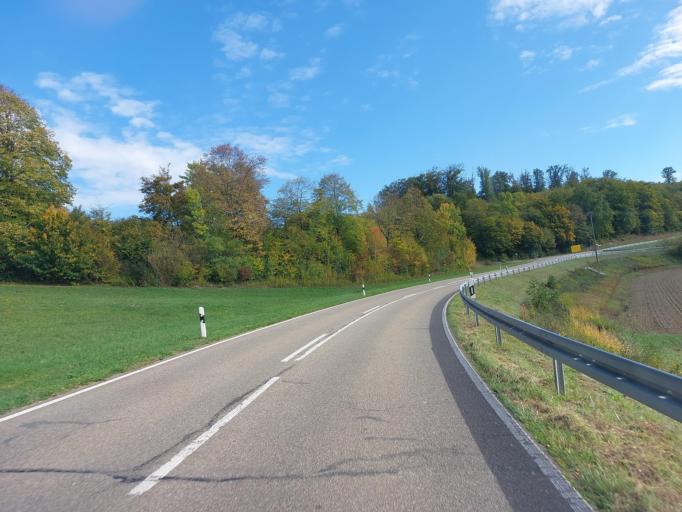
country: DE
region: Baden-Wuerttemberg
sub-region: Freiburg Region
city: Malterdingen
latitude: 48.1744
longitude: 7.8192
